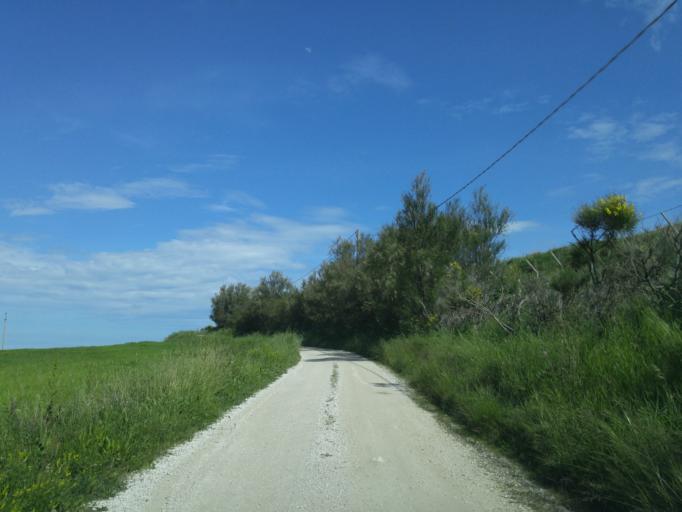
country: IT
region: The Marches
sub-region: Provincia di Pesaro e Urbino
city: San Costanzo
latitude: 43.7905
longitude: 13.0617
